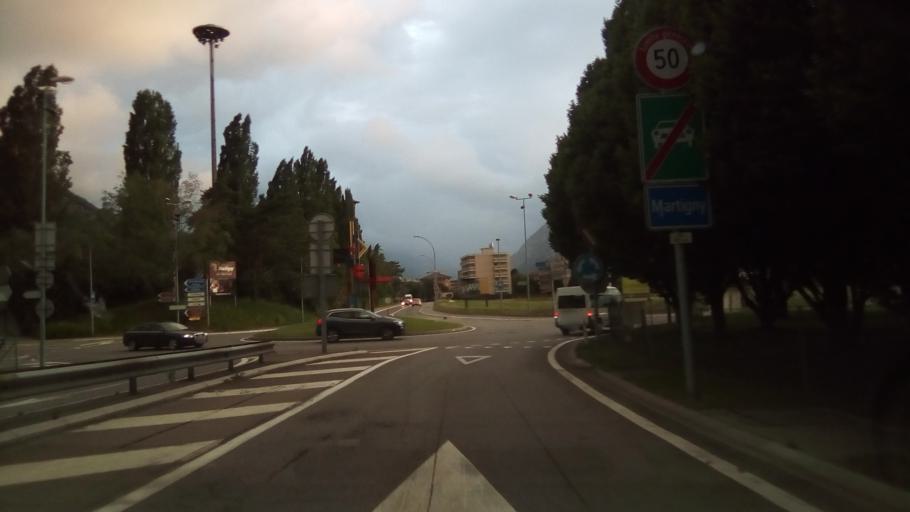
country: CH
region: Valais
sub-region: Martigny District
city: Martigny-Ville
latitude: 46.0994
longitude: 7.0834
